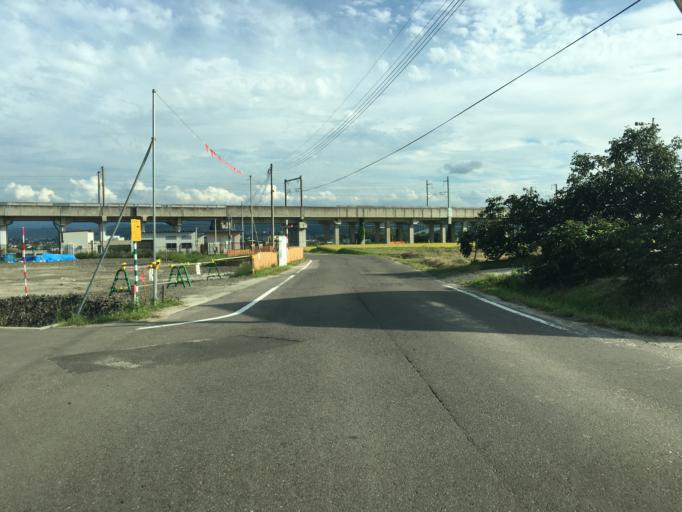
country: JP
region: Fukushima
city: Hobaramachi
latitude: 37.8333
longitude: 140.4981
